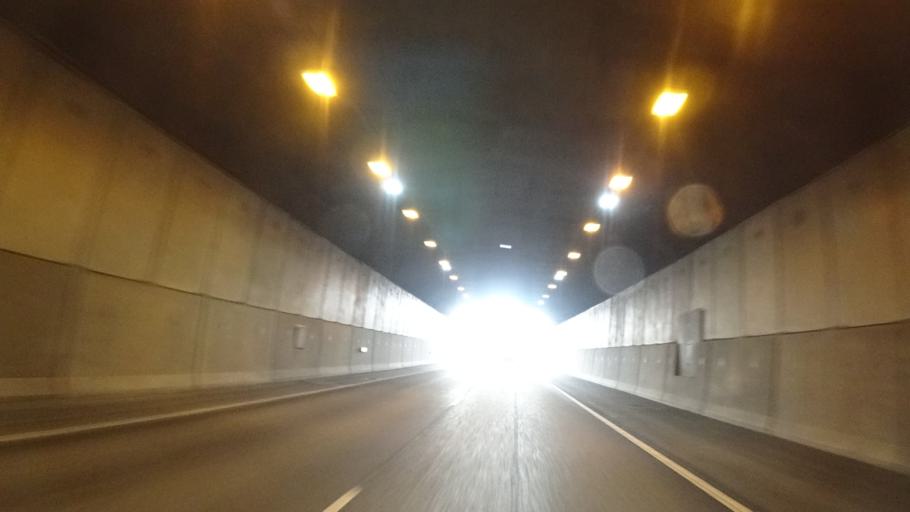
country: FI
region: Uusimaa
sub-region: Loviisa
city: Ruotsinpyhtaeae
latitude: 60.4931
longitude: 26.4381
